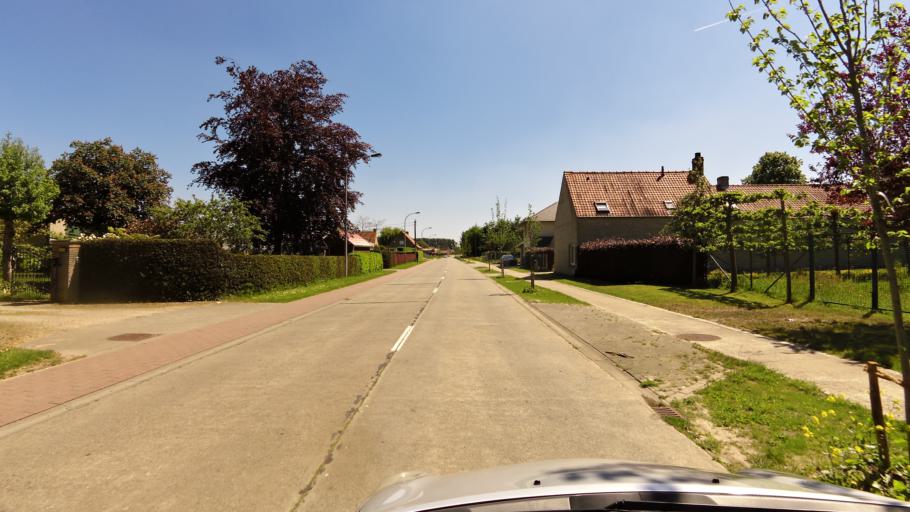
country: BE
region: Flanders
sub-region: Provincie West-Vlaanderen
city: Oostkamp
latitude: 51.1241
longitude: 3.2655
